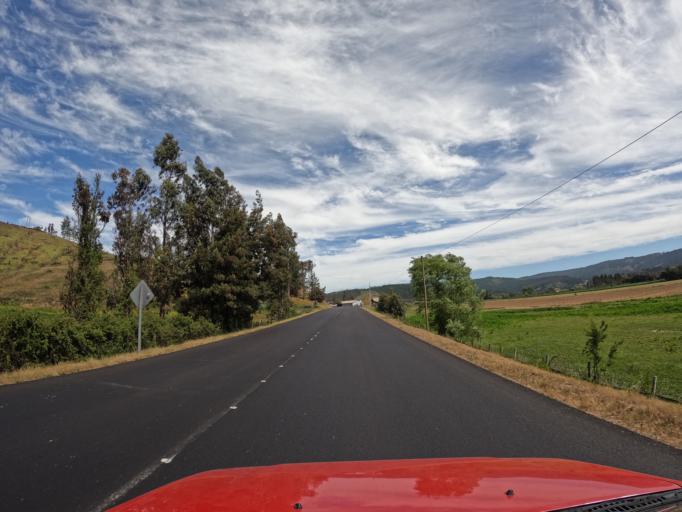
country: CL
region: Maule
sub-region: Provincia de Talca
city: Constitucion
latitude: -35.0743
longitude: -72.0395
